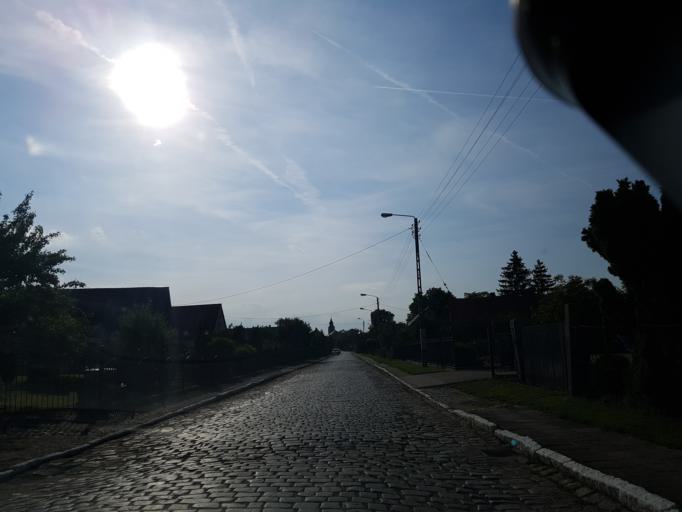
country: PL
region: Lower Silesian Voivodeship
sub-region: Powiat strzelinski
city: Wiazow
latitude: 50.8414
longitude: 17.2166
